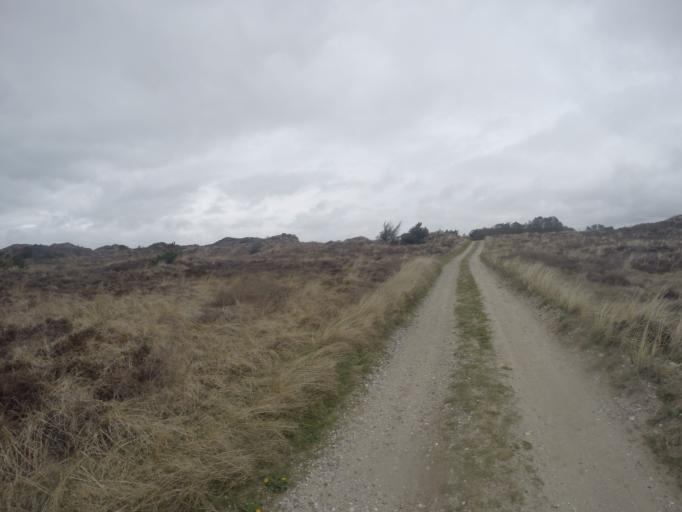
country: DK
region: North Denmark
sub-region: Thisted Kommune
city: Hurup
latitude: 56.8812
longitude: 8.3177
